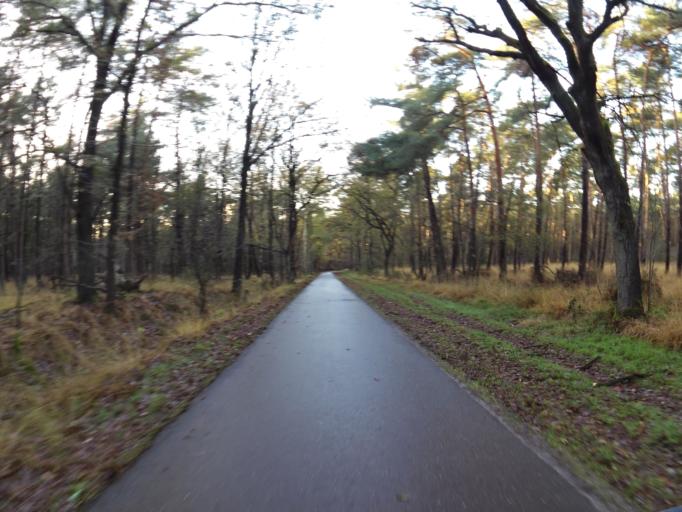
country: NL
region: North Brabant
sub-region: Gemeente Waalwijk
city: Waalwijk
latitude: 51.6612
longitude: 5.1034
